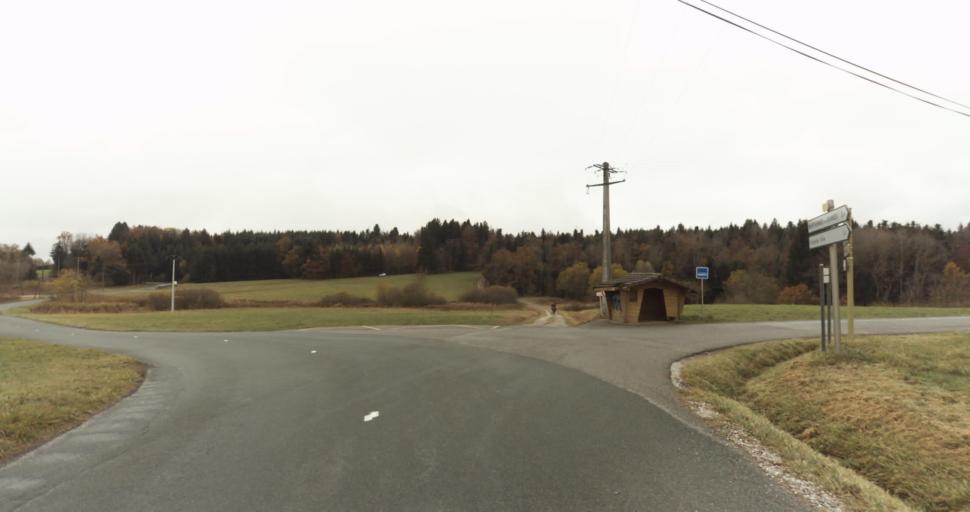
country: FR
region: Rhone-Alpes
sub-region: Departement de la Haute-Savoie
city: Groisy
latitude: 46.0305
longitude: 6.1831
